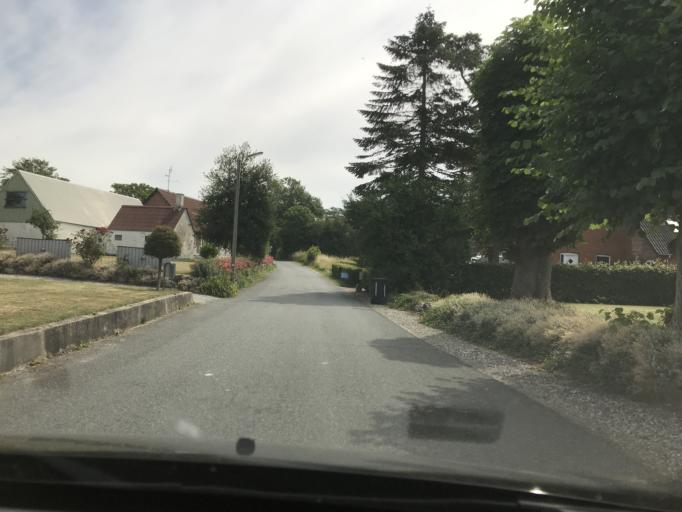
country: DK
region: South Denmark
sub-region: AEro Kommune
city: AEroskobing
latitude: 54.9127
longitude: 10.2828
